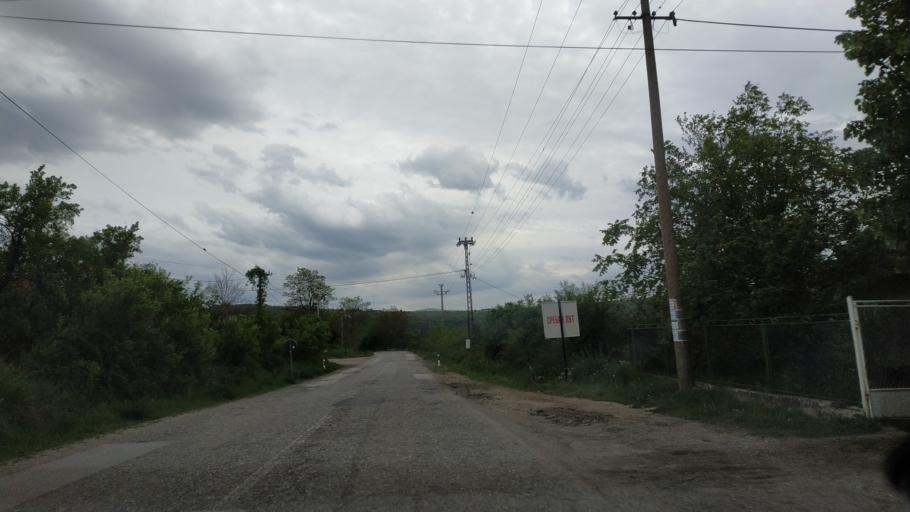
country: RS
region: Central Serbia
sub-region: Nisavski Okrug
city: Aleksinac
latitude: 43.6027
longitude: 21.6868
